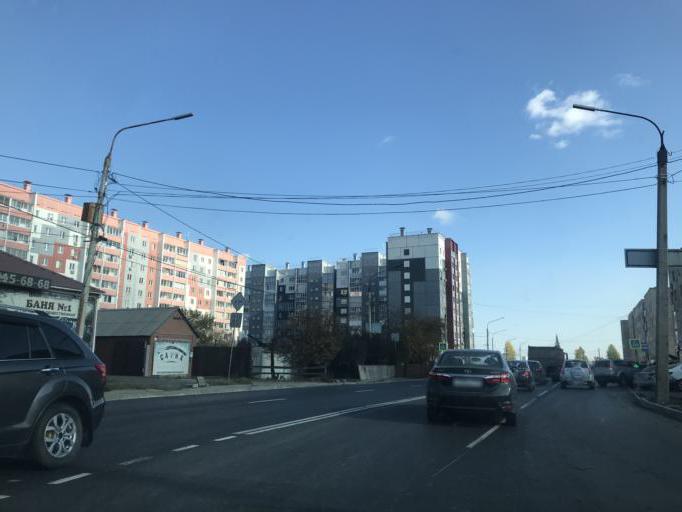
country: RU
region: Chelyabinsk
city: Roshchino
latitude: 55.2354
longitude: 61.2977
